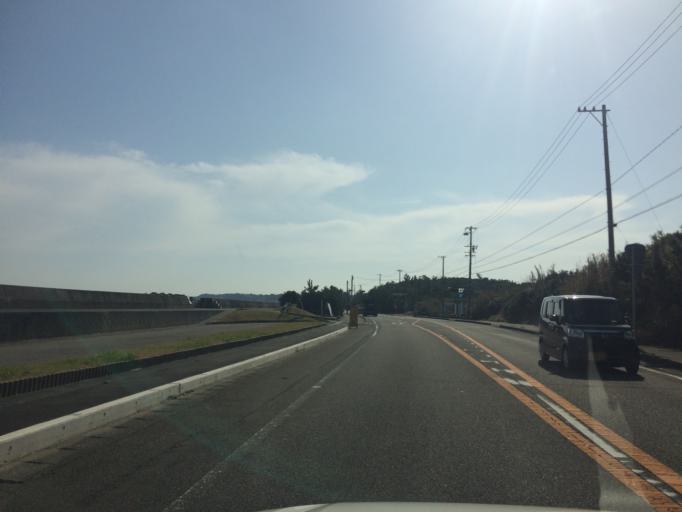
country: JP
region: Shizuoka
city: Sagara
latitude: 34.6437
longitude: 138.1930
